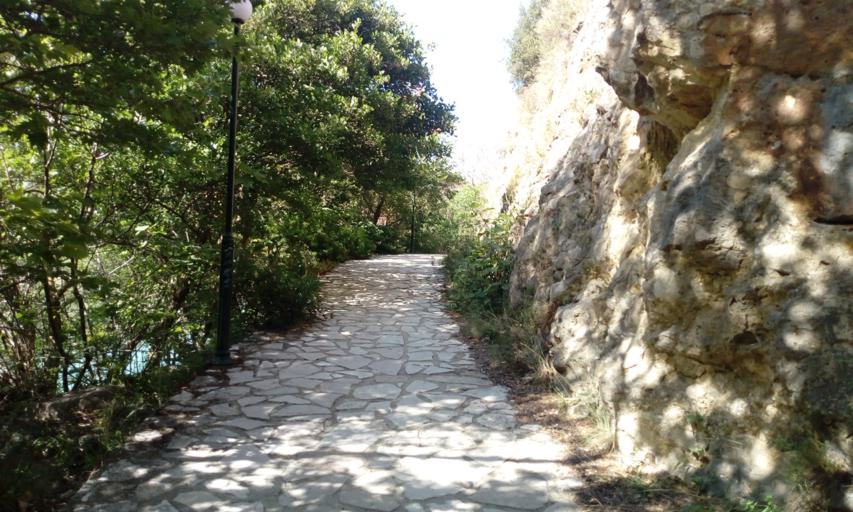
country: GR
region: Epirus
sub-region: Nomos Prevezis
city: Kanalaki
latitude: 39.3285
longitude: 20.6198
